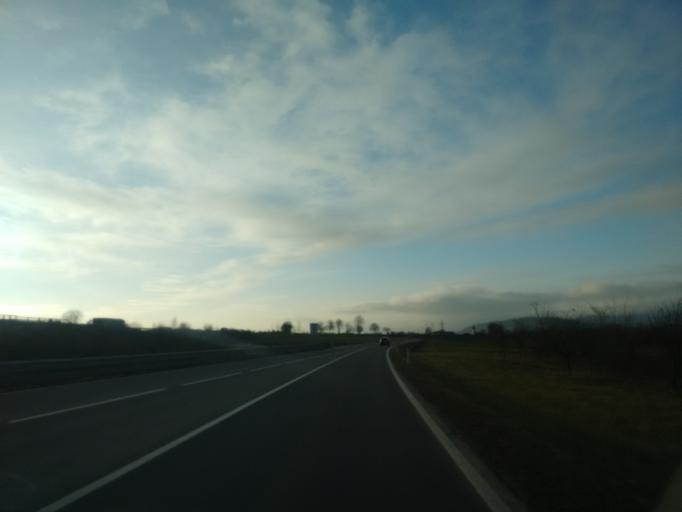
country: AT
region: Lower Austria
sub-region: Politischer Bezirk Melk
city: Melk
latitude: 48.2163
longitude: 15.2974
